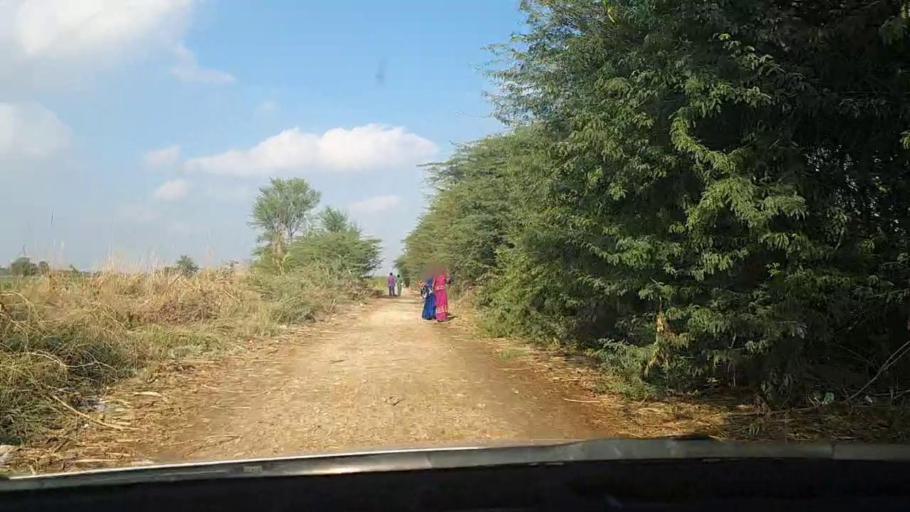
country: PK
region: Sindh
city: Tando Mittha Khan
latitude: 25.8788
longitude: 69.2928
